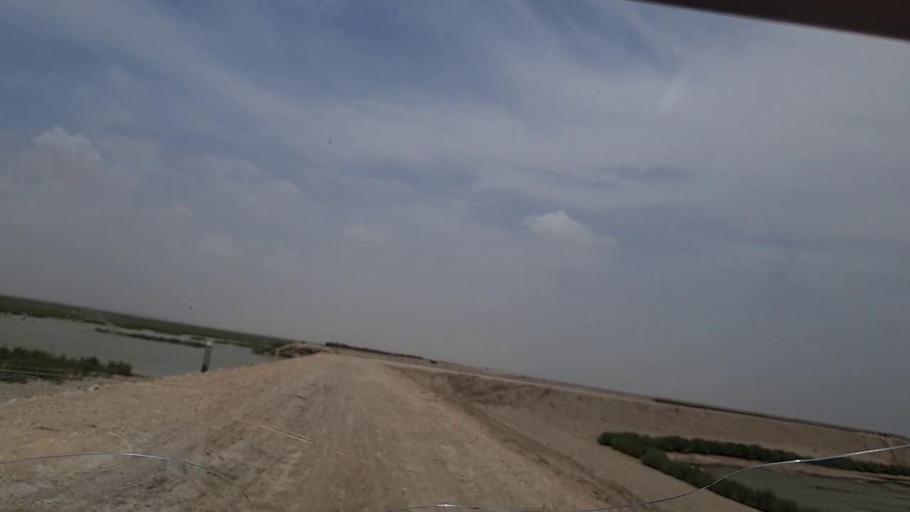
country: PK
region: Sindh
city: Bhan
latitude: 26.5090
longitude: 67.6266
